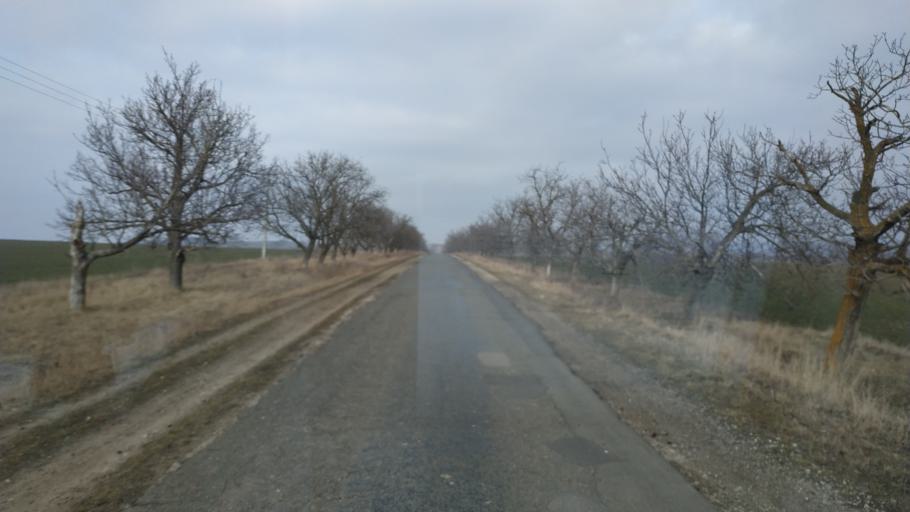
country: MD
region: Hincesti
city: Dancu
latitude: 46.8664
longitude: 28.2927
